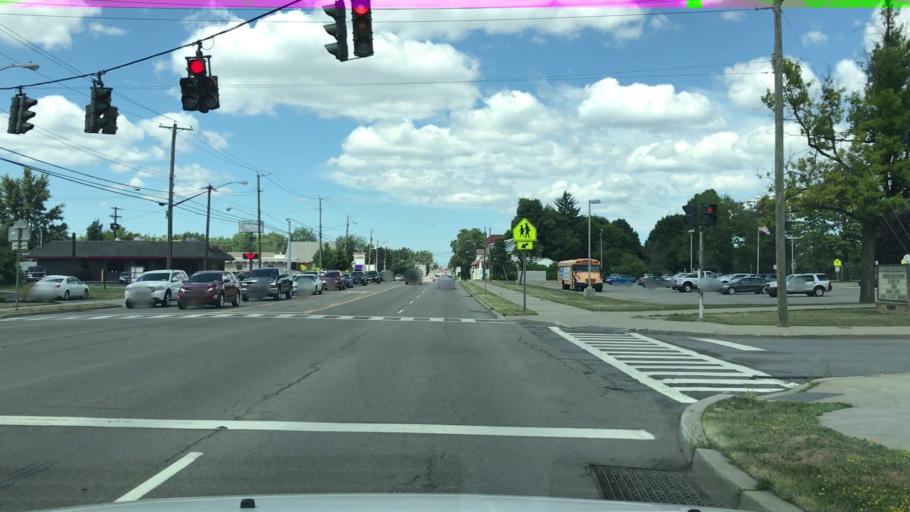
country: US
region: New York
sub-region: Erie County
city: Depew
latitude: 42.8958
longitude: -78.6969
